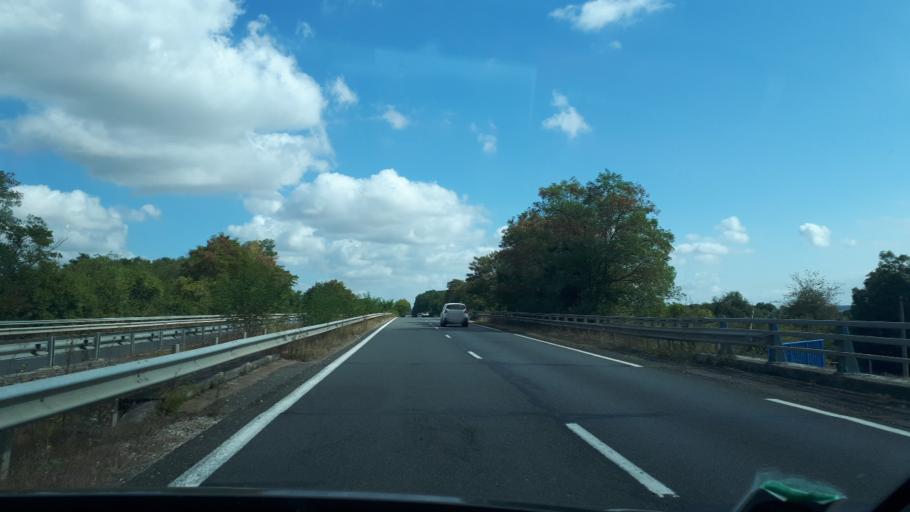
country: FR
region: Centre
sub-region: Departement du Loir-et-Cher
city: Saint-Ouen
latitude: 47.8295
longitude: 1.0810
